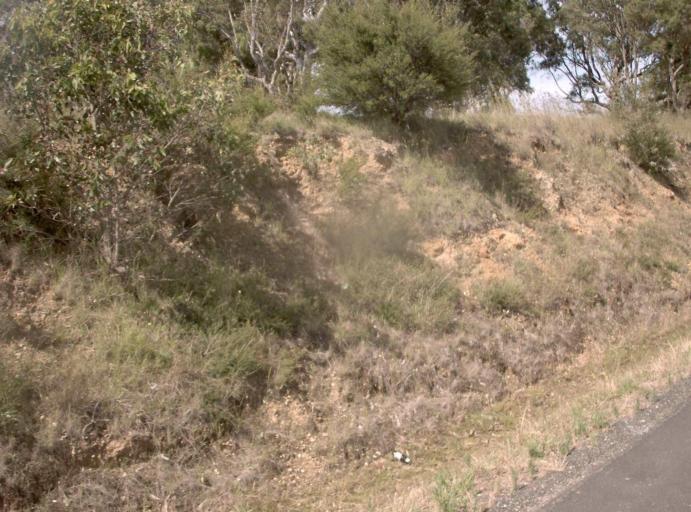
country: AU
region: Victoria
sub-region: East Gippsland
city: Bairnsdale
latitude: -37.8157
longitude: 147.7537
